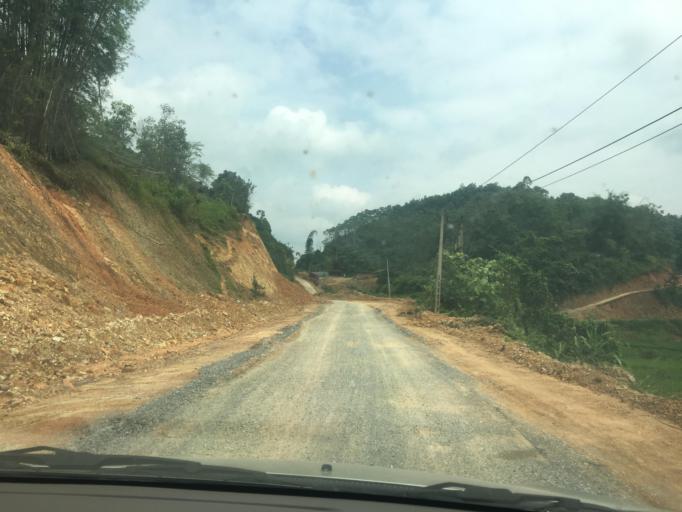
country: VN
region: Bac Kan
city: Yen Lac
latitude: 22.1613
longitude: 106.3062
